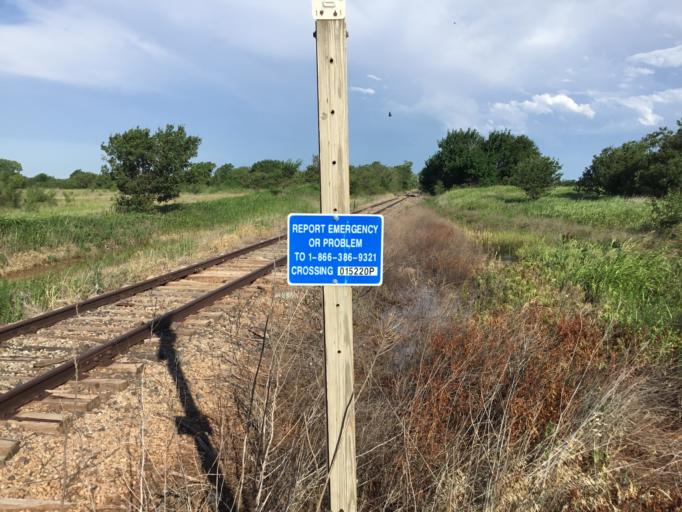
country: US
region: Kansas
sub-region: Kingman County
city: Kingman
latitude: 37.6135
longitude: -97.9539
